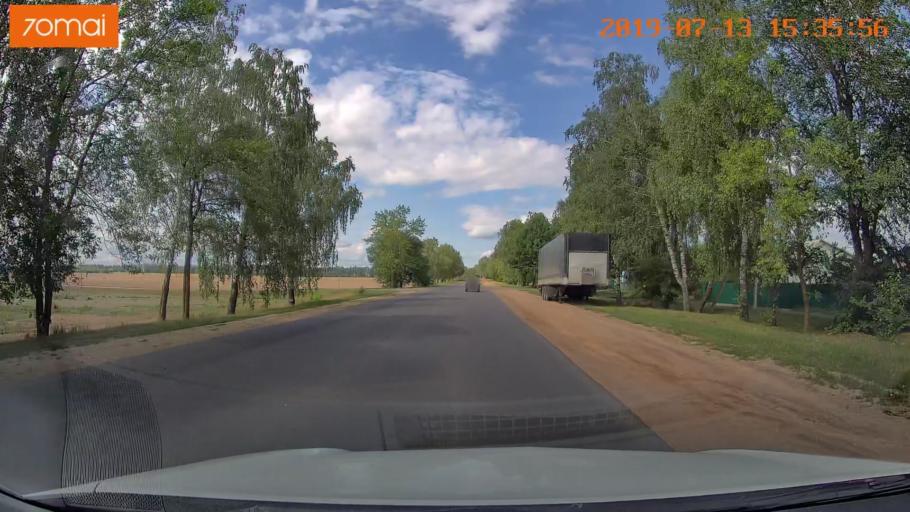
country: BY
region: Mogilev
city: Babruysk
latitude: 53.1269
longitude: 29.1667
